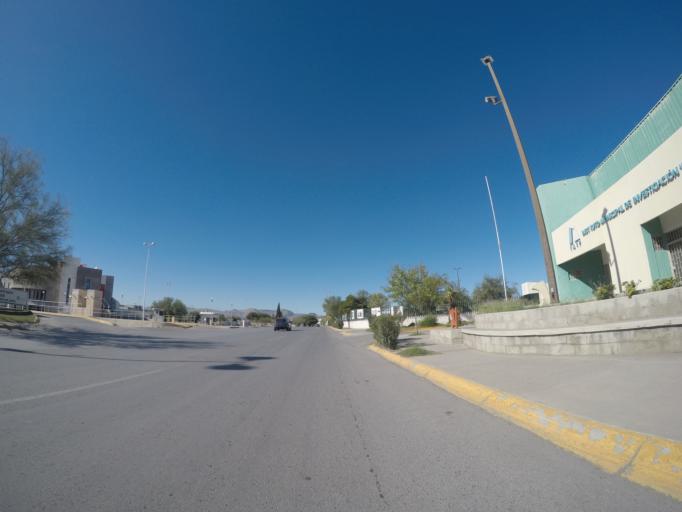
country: MX
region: Chihuahua
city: Ciudad Juarez
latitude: 31.7445
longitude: -106.4456
